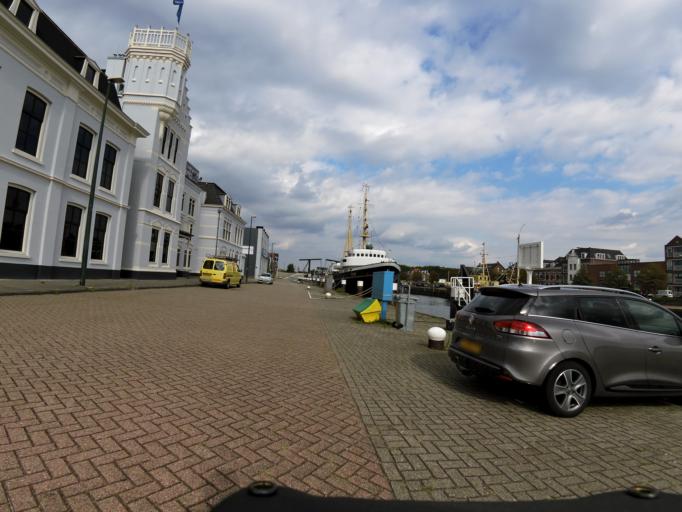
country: NL
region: South Holland
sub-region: Gemeente Maassluis
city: Maassluis
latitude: 51.9162
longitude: 4.2462
